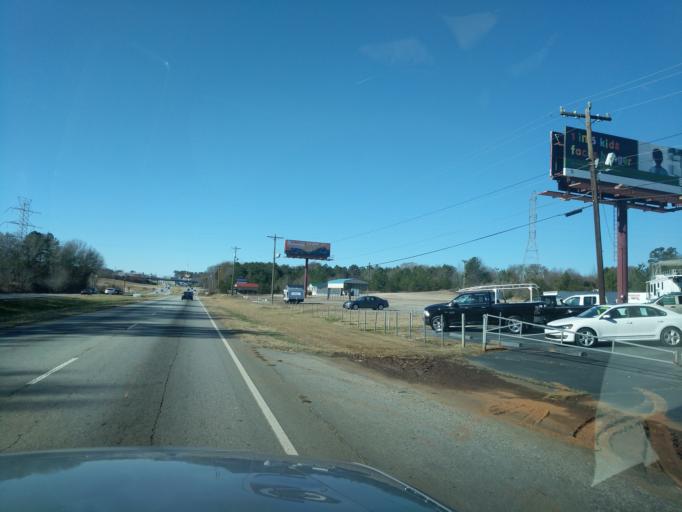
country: US
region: South Carolina
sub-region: Anderson County
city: Powdersville
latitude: 34.8297
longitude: -82.5188
